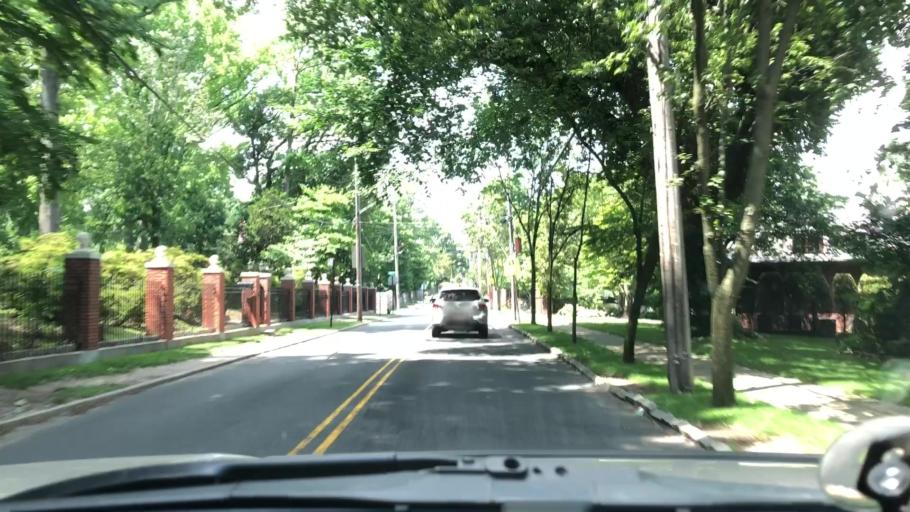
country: US
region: New Jersey
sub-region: Hudson County
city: Bayonne
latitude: 40.6252
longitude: -74.0886
